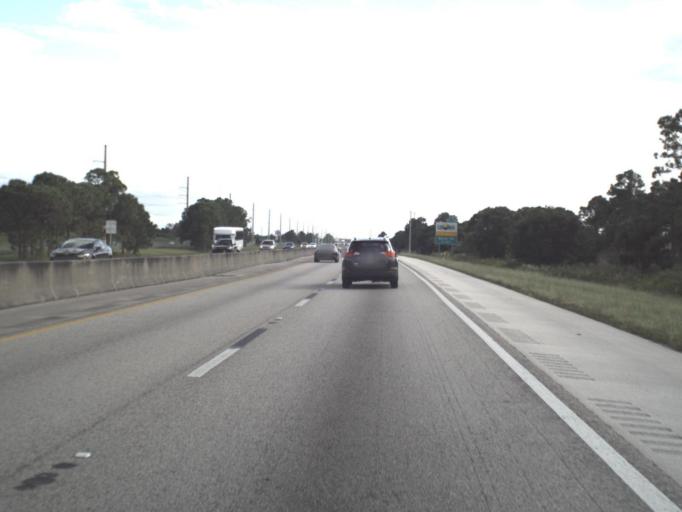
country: US
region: Florida
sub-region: Martin County
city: North River Shores
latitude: 27.2236
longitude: -80.3405
